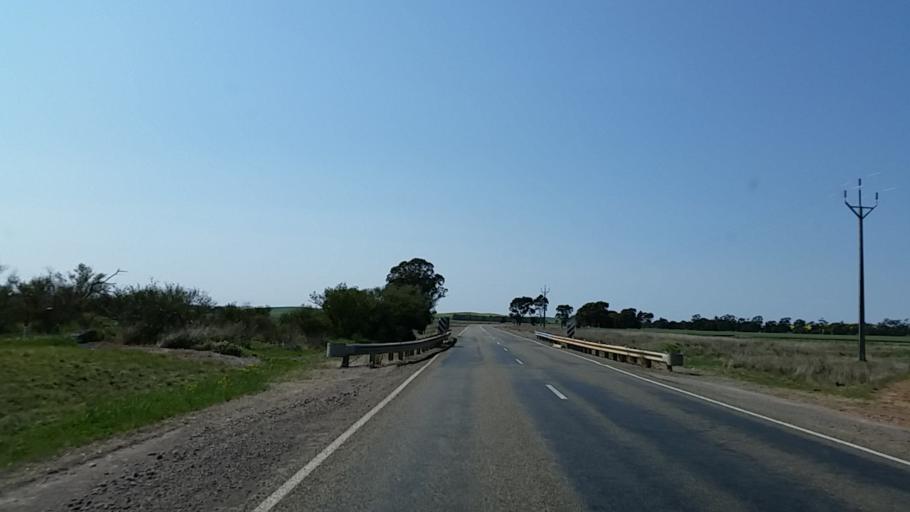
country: AU
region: South Australia
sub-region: Northern Areas
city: Jamestown
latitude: -33.1863
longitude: 138.4995
